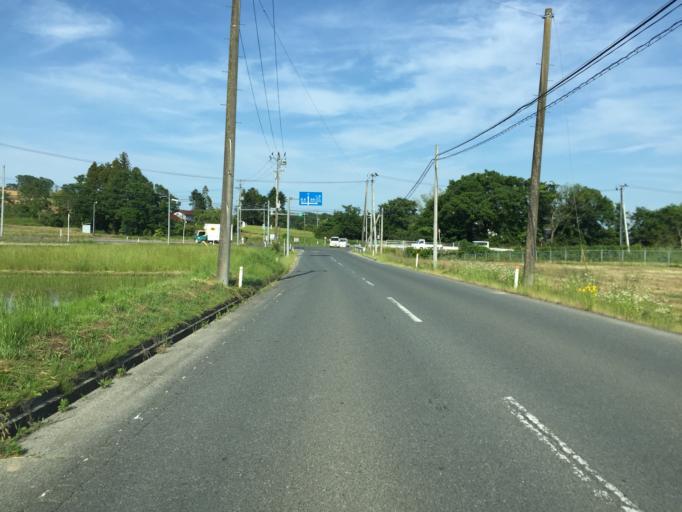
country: JP
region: Fukushima
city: Namie
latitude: 37.6638
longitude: 140.9616
